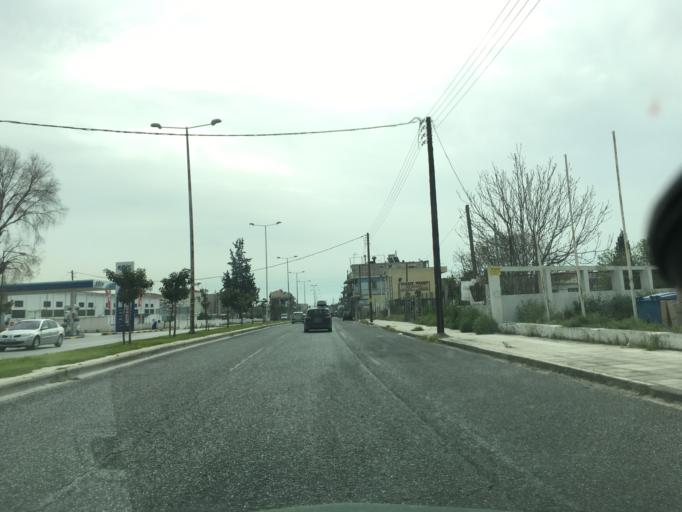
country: GR
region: Thessaly
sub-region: Nomos Magnisias
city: Nea Ionia
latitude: 39.3691
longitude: 22.9186
